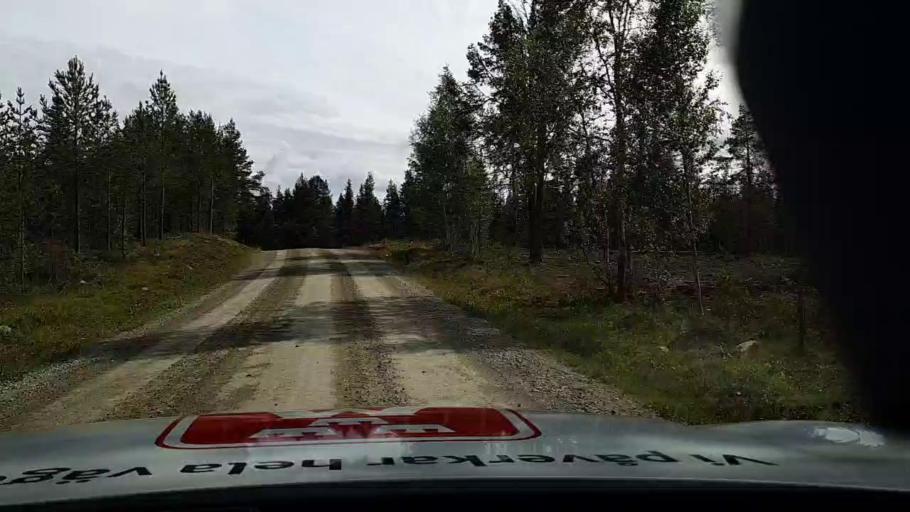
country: SE
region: Jaemtland
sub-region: Are Kommun
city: Jarpen
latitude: 62.5148
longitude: 13.4882
